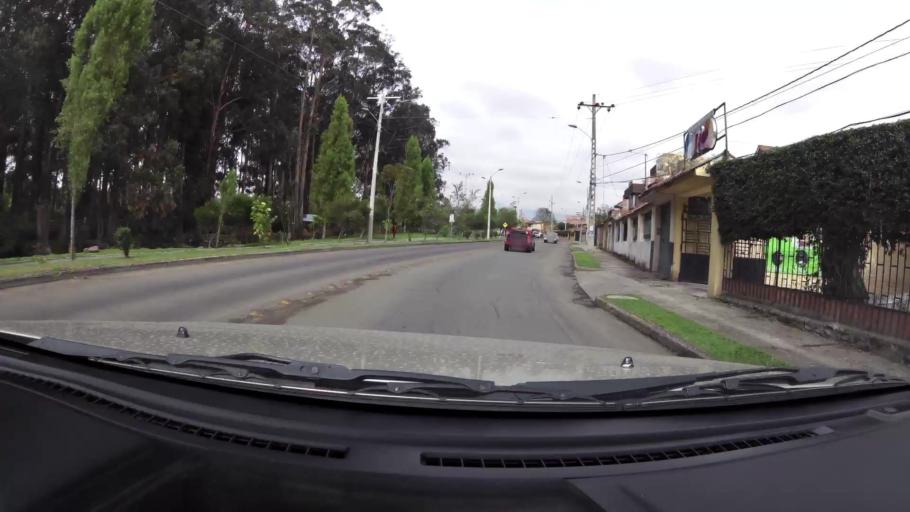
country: EC
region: Azuay
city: Cuenca
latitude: -2.9080
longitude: -78.9853
